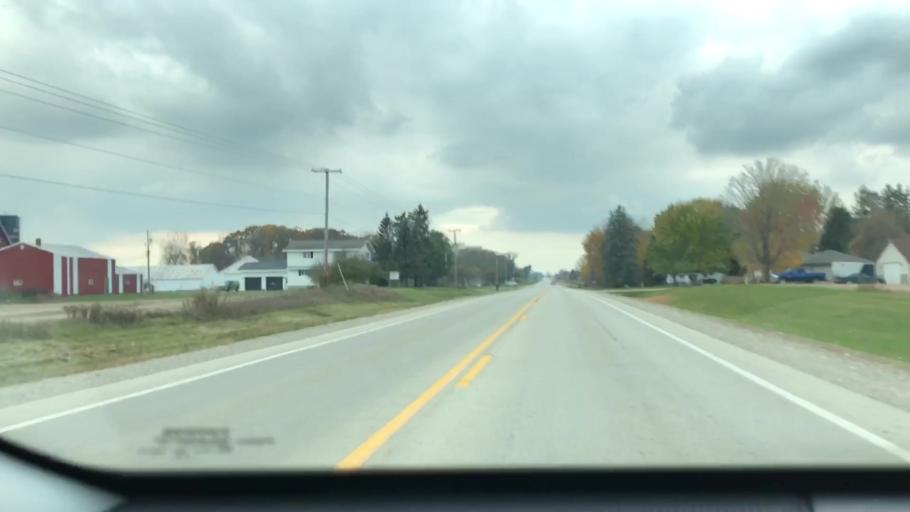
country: US
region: Wisconsin
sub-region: Outagamie County
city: Seymour
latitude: 44.5014
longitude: -88.2679
